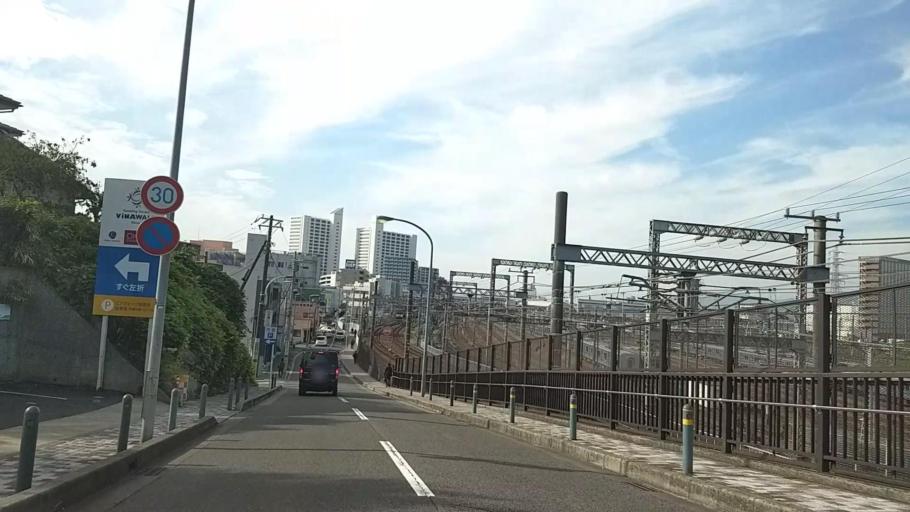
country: JP
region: Kanagawa
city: Zama
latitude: 35.4566
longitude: 139.3955
